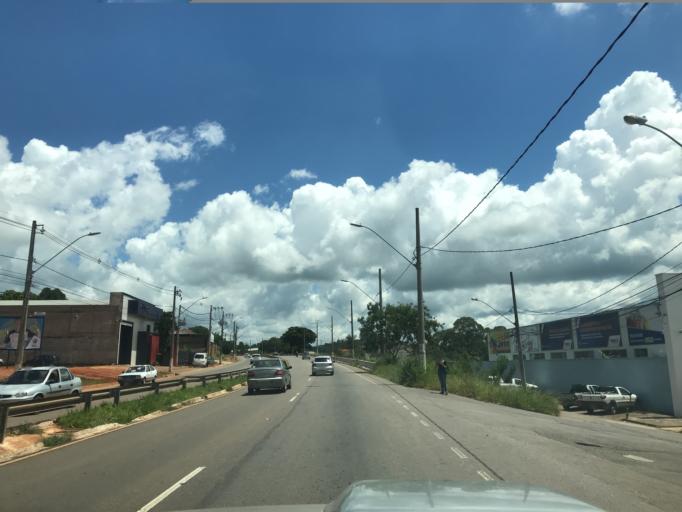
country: BR
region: Minas Gerais
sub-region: Tres Coracoes
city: Tres Coracoes
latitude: -21.6694
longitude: -45.2732
